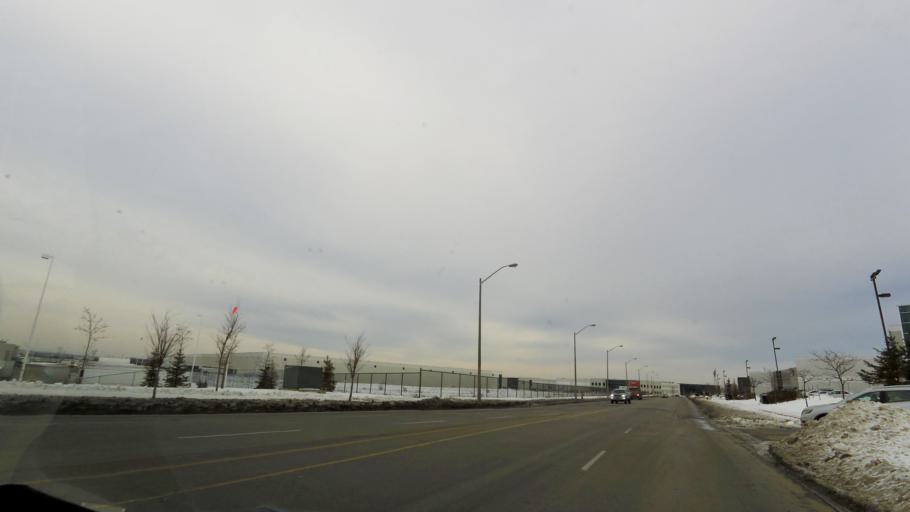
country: CA
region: Ontario
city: Etobicoke
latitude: 43.7794
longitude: -79.6478
